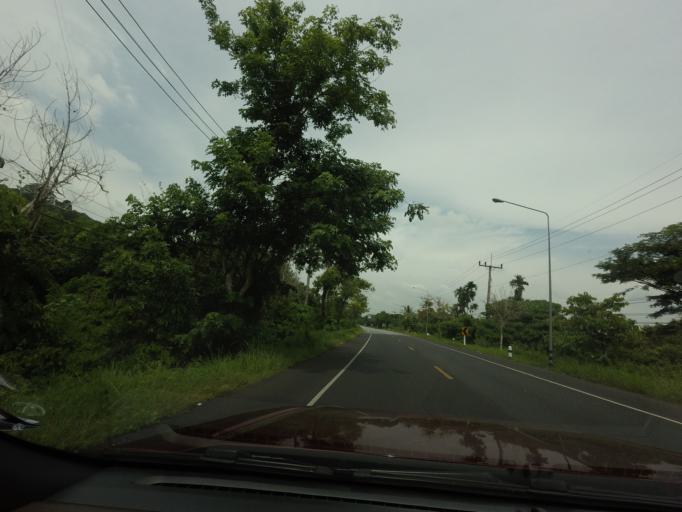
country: TH
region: Pattani
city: Mae Lan
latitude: 6.6377
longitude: 101.3022
